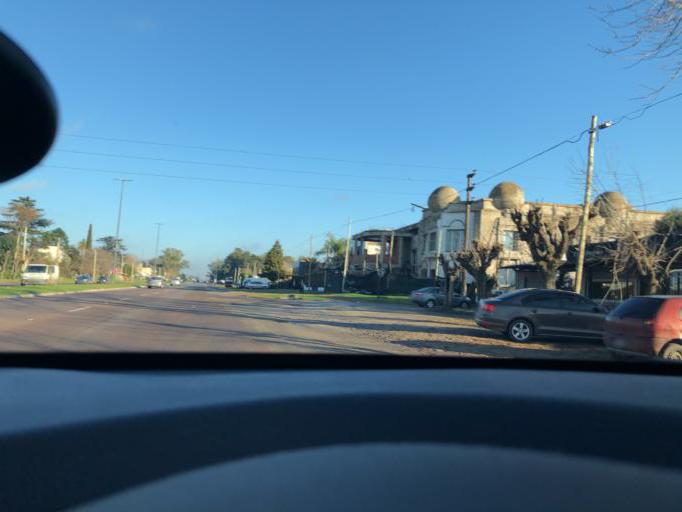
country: AR
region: Buenos Aires
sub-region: Partido de La Plata
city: La Plata
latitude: -34.8532
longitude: -58.0807
